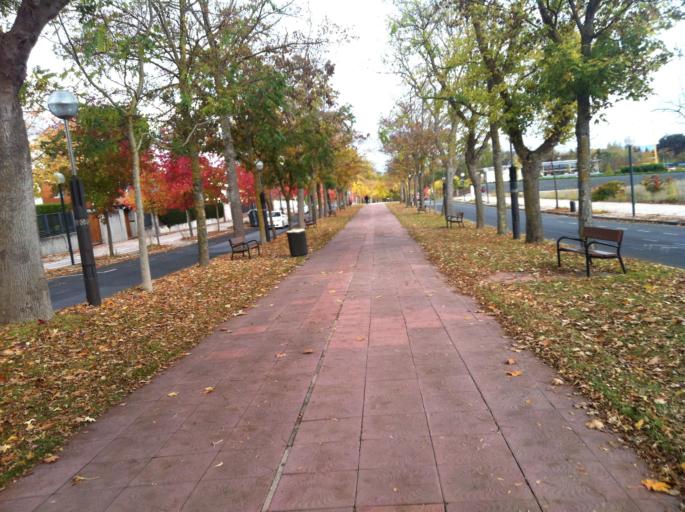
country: ES
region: Basque Country
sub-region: Provincia de Alava
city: Gasteiz / Vitoria
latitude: 42.8349
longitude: -2.6955
